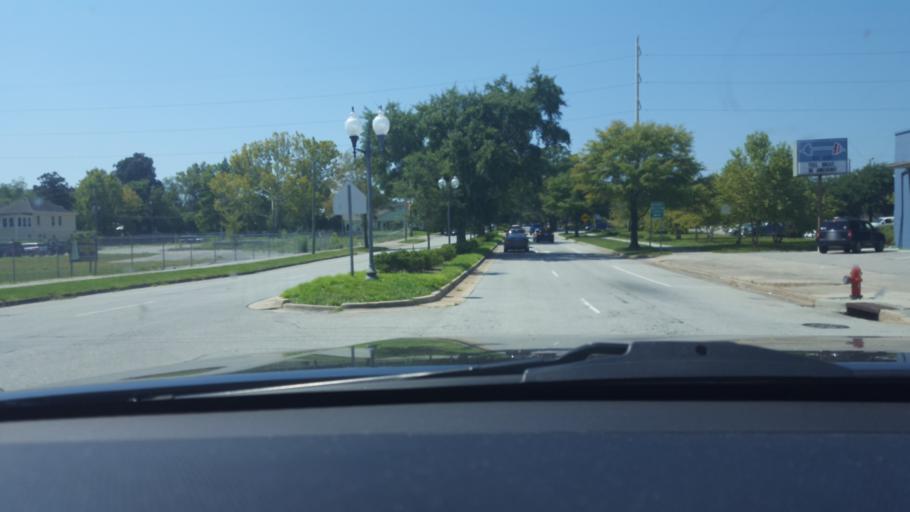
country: US
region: North Carolina
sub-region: New Hanover County
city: Wilmington
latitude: 34.2365
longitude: -77.9354
